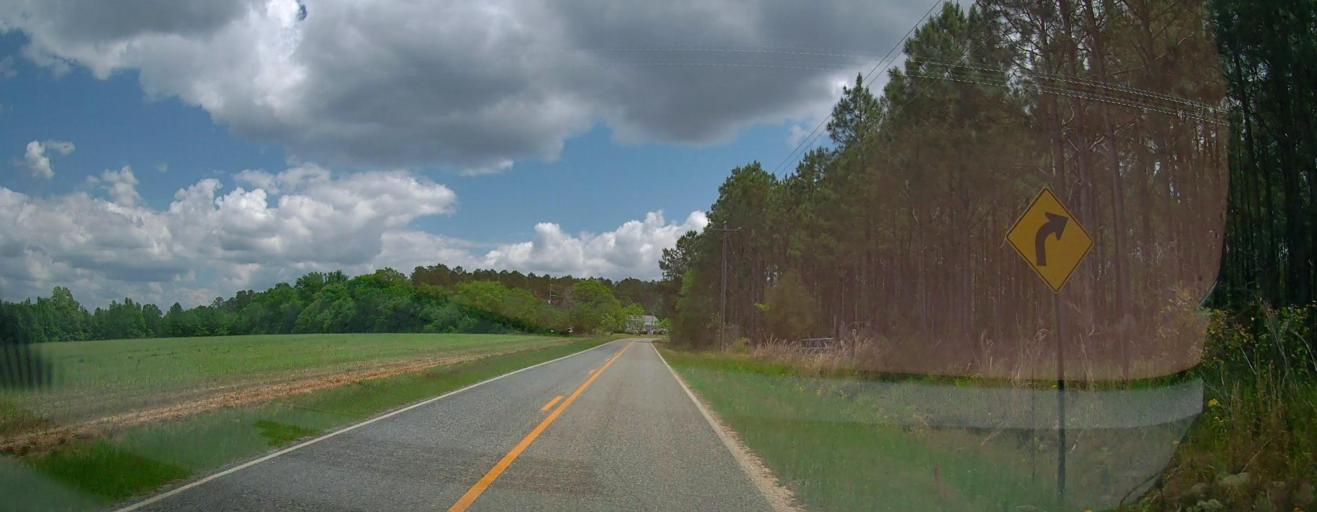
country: US
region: Georgia
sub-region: Laurens County
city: East Dublin
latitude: 32.5871
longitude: -82.7890
